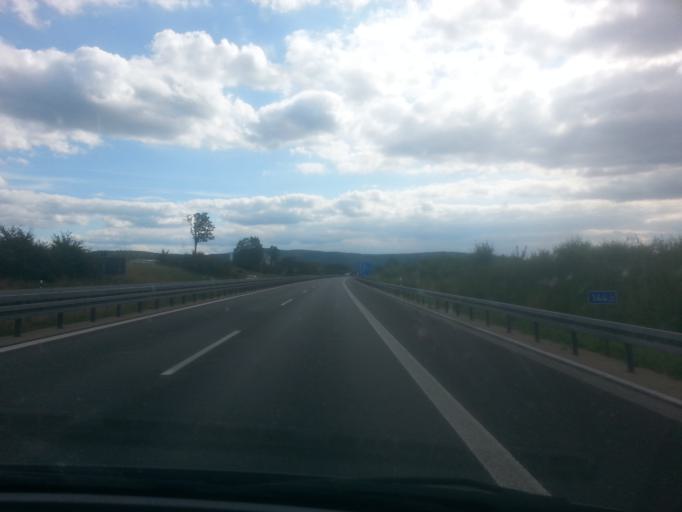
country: DE
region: Bavaria
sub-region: Upper Palatinate
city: Nabburg
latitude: 49.4628
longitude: 12.1949
